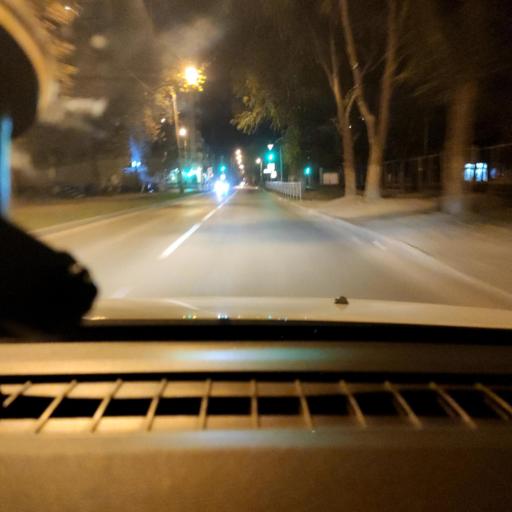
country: RU
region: Samara
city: Samara
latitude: 53.1905
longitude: 50.1841
